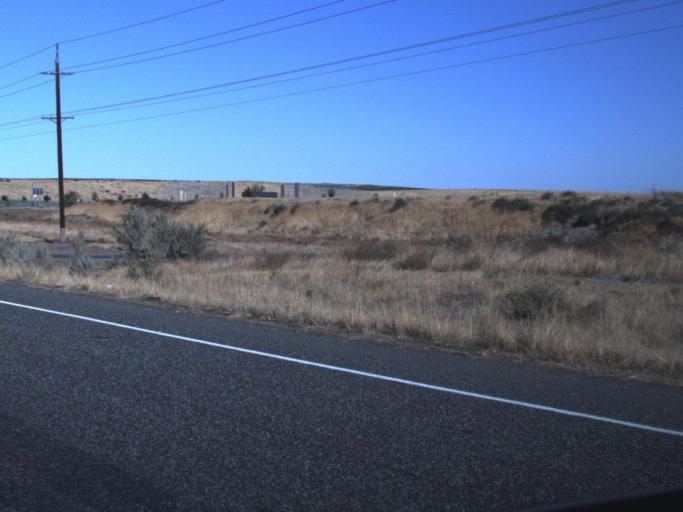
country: US
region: Washington
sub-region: Benton County
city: West Richland
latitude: 46.3275
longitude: -119.3204
